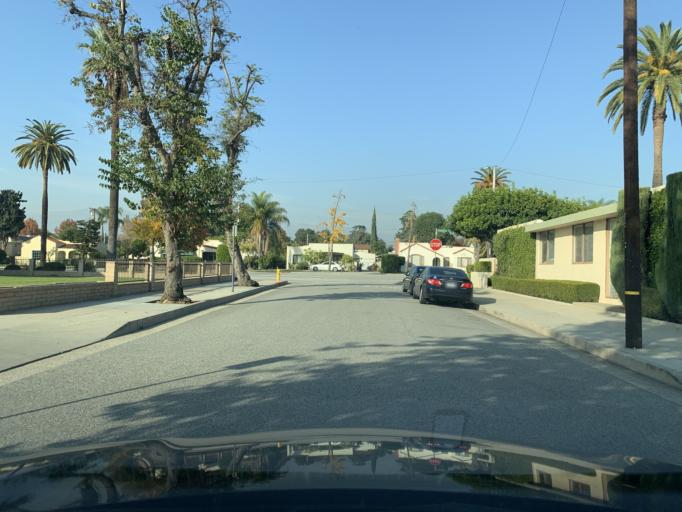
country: US
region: California
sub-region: Los Angeles County
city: Covina
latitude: 34.0858
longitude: -117.8967
